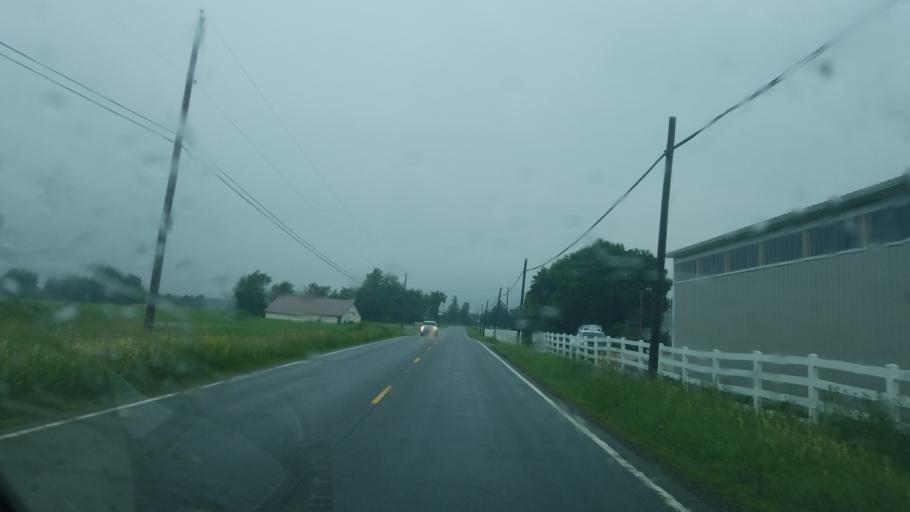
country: US
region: Ohio
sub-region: Richland County
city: Shelby
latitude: 40.9269
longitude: -82.6600
